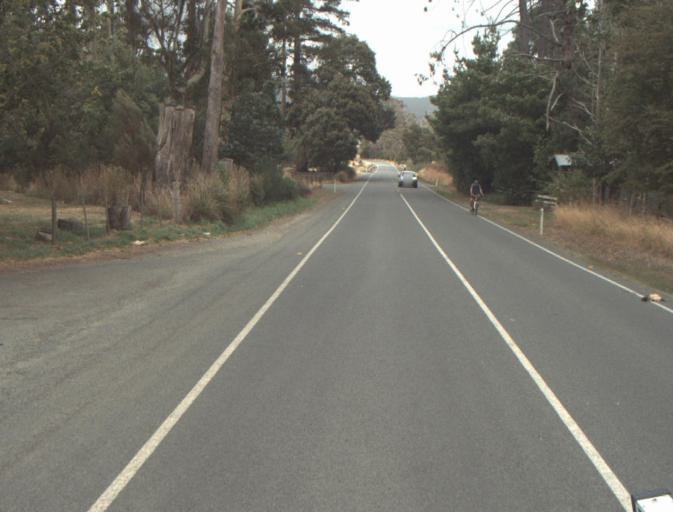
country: AU
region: Tasmania
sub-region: Launceston
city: Mayfield
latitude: -41.2295
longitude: 147.2091
